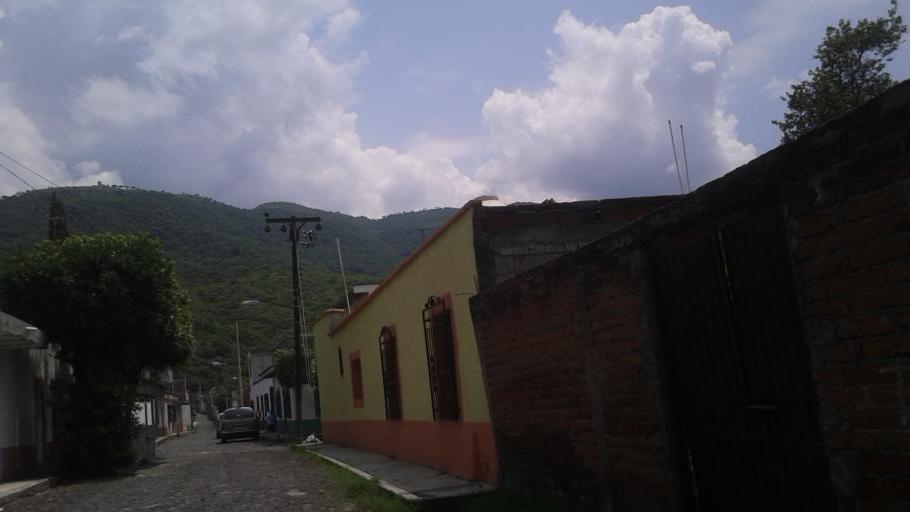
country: MX
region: Nayarit
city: Jala
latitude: 21.1043
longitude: -104.4421
